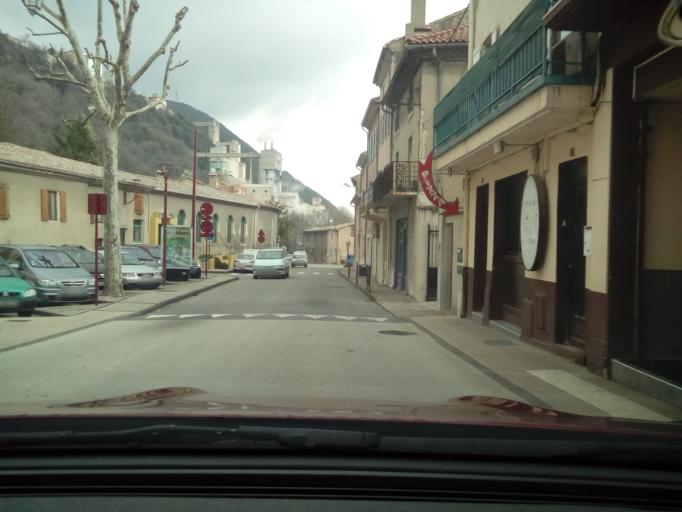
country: FR
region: Rhone-Alpes
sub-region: Departement de l'Ardeche
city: Cruas
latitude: 44.6572
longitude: 4.7626
